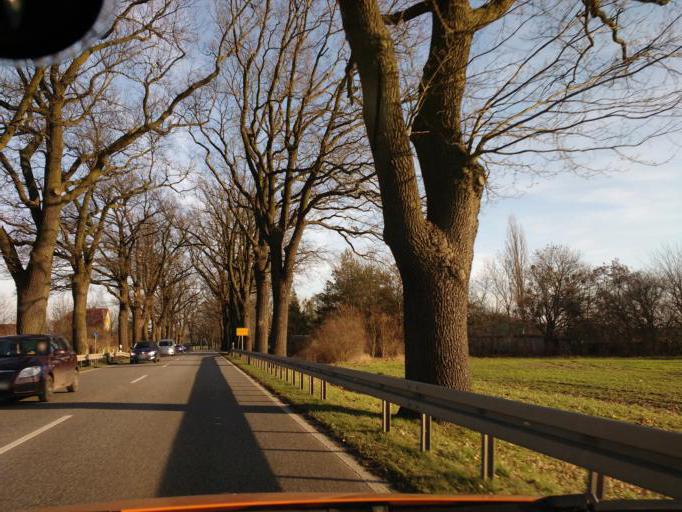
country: DE
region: Brandenburg
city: Werneuchen
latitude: 52.6301
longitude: 13.7196
